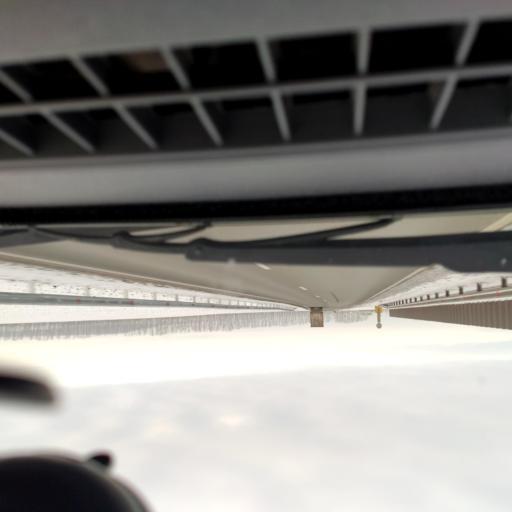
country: RU
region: Bashkortostan
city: Asanovo
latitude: 54.9509
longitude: 55.5839
